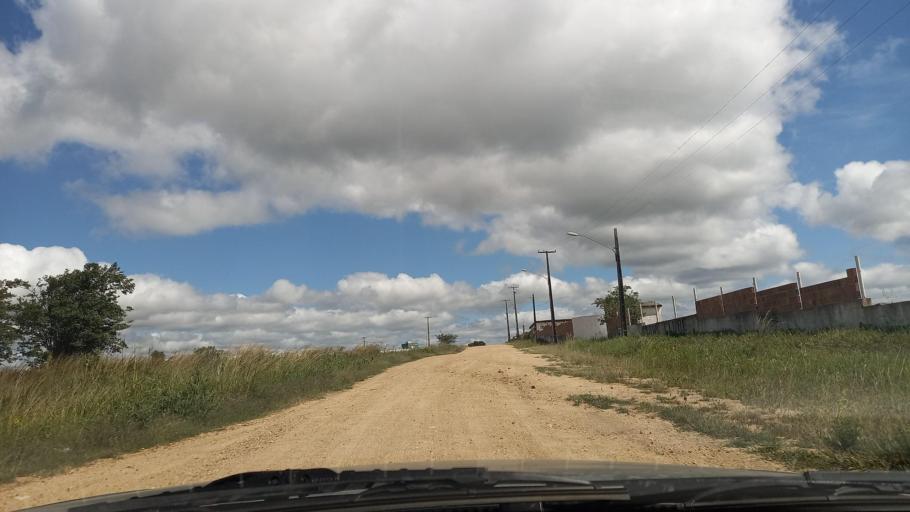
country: BR
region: Pernambuco
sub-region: Caruaru
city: Caruaru
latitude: -8.2324
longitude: -35.9825
